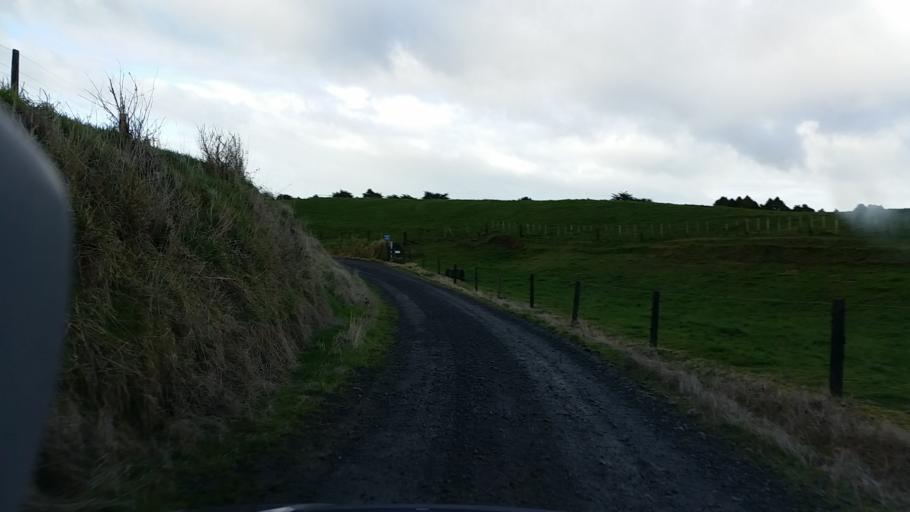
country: NZ
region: Taranaki
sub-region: South Taranaki District
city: Eltham
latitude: -39.3312
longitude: 174.1722
